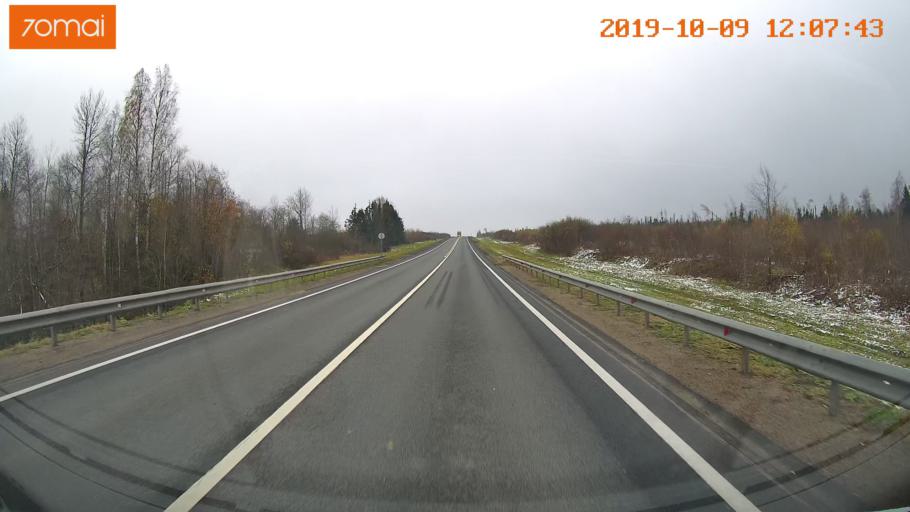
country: RU
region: Jaroslavl
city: Prechistoye
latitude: 58.5958
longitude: 40.3435
